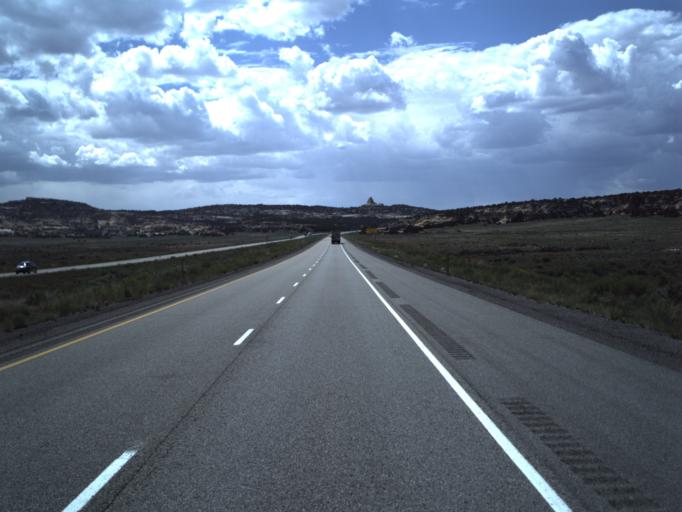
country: US
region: Utah
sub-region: Emery County
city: Castle Dale
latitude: 38.8684
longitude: -110.7792
